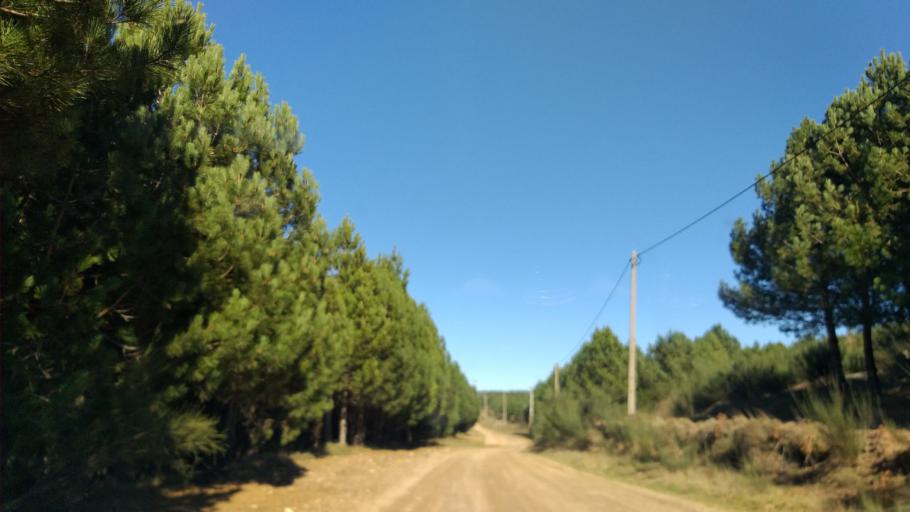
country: PT
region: Guarda
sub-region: Manteigas
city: Manteigas
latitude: 40.5110
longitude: -7.4596
